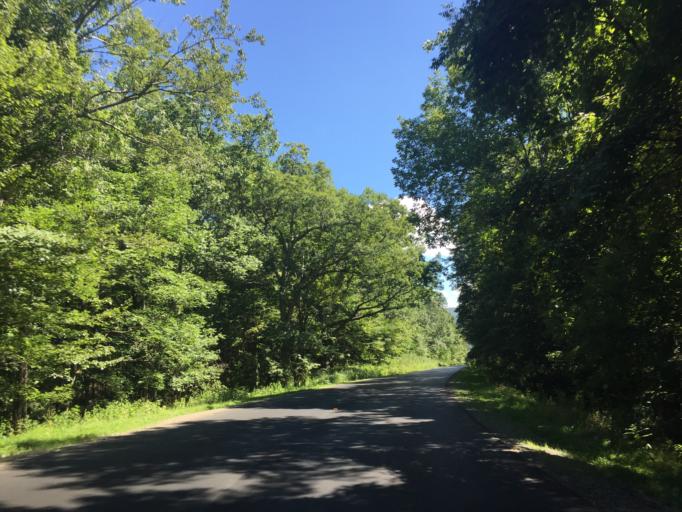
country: US
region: Virginia
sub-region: Page County
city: Luray
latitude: 38.6736
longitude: -78.3326
